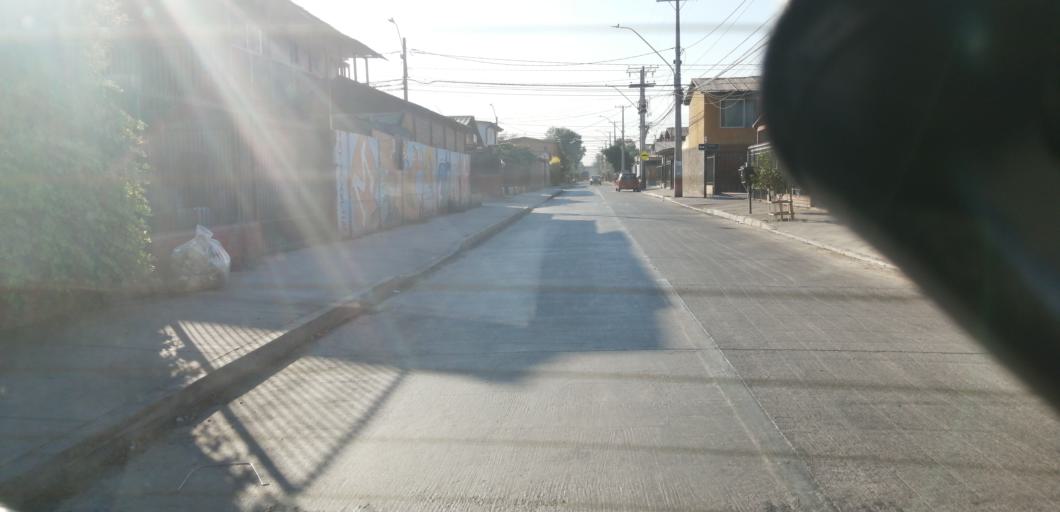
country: CL
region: Santiago Metropolitan
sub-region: Provincia de Santiago
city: Lo Prado
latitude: -33.4580
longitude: -70.7453
